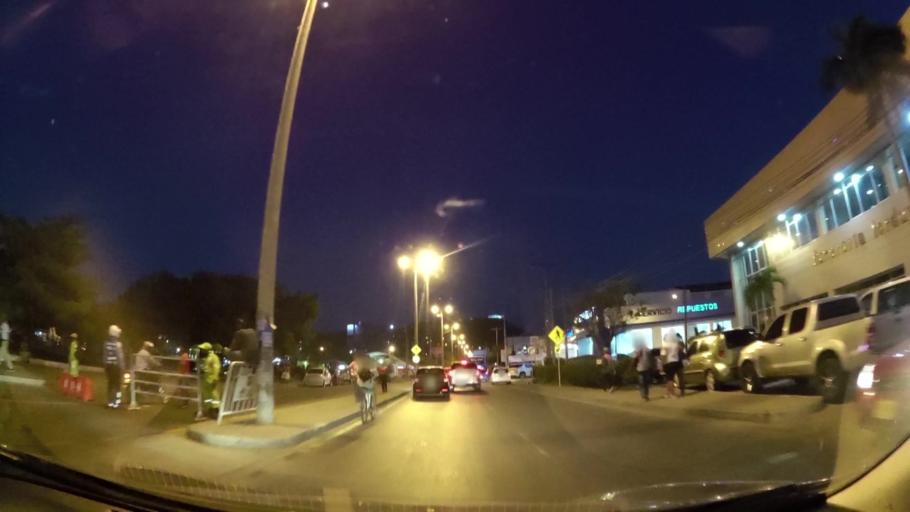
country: CO
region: Bolivar
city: Cartagena
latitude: 10.4209
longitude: -75.5381
